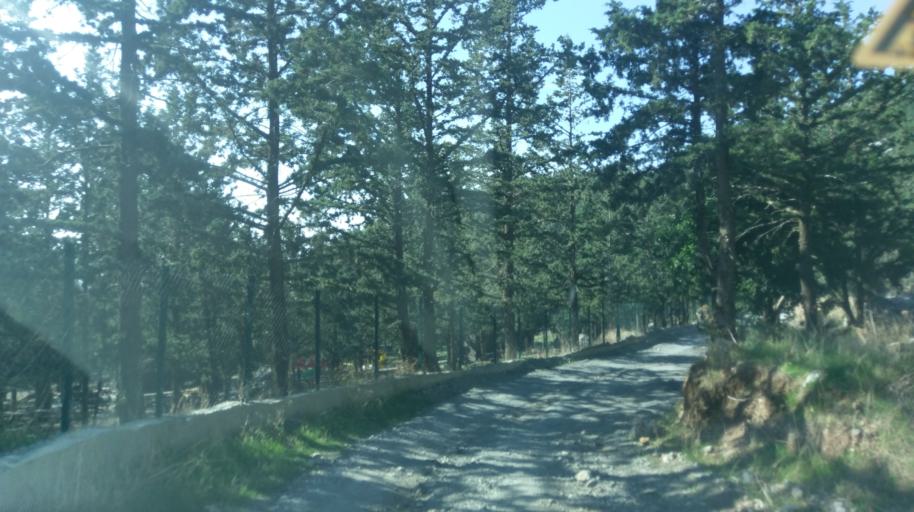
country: CY
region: Keryneia
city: Kyrenia
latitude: 35.2861
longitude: 33.3885
